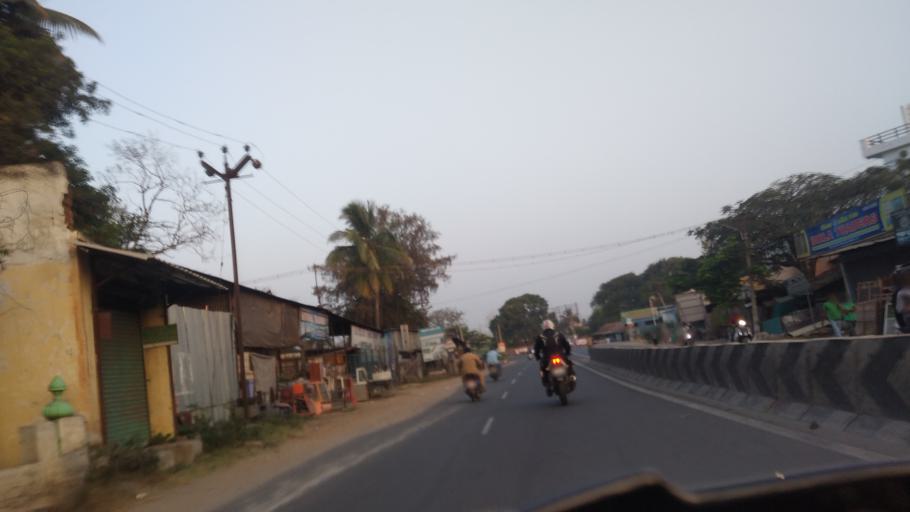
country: IN
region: Tamil Nadu
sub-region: Coimbatore
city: Coimbatore
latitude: 10.9719
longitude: 76.9656
